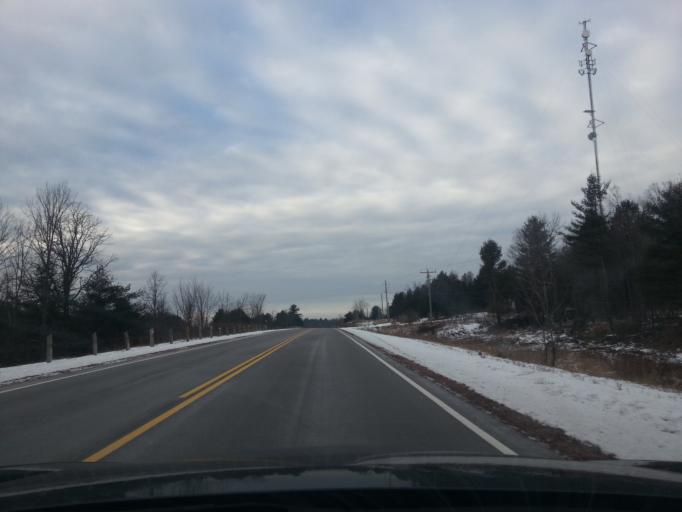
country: CA
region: Ontario
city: Skatepark
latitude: 44.7063
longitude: -77.0015
